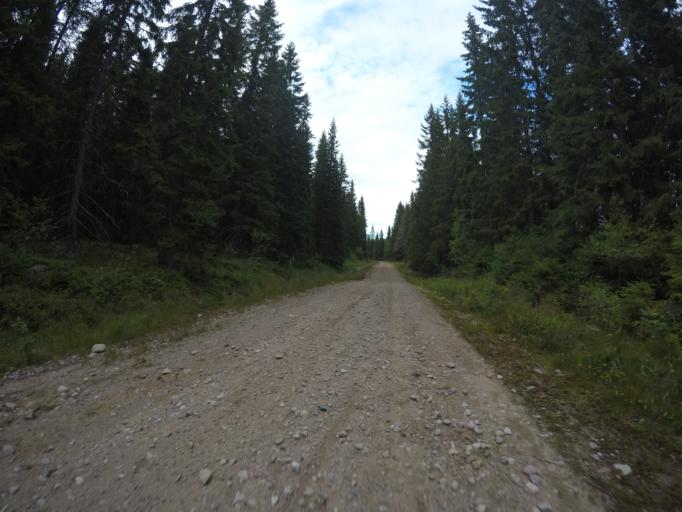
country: SE
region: OErebro
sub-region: Hallefors Kommun
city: Haellefors
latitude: 60.0292
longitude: 14.4700
